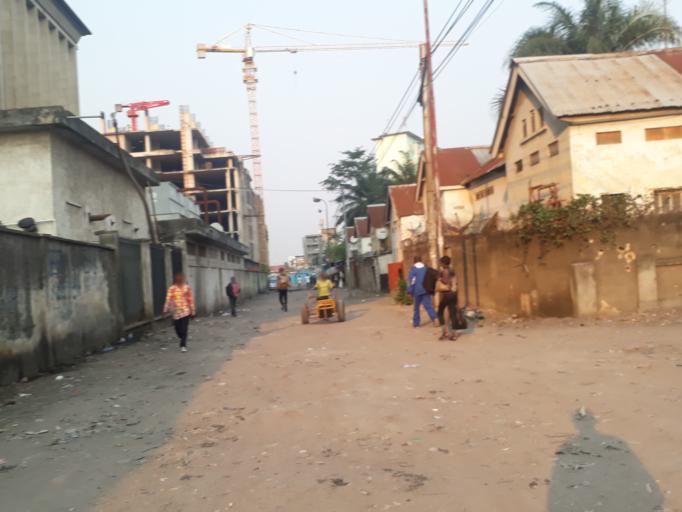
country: CD
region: Kinshasa
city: Kinshasa
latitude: -4.3031
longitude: 15.3147
